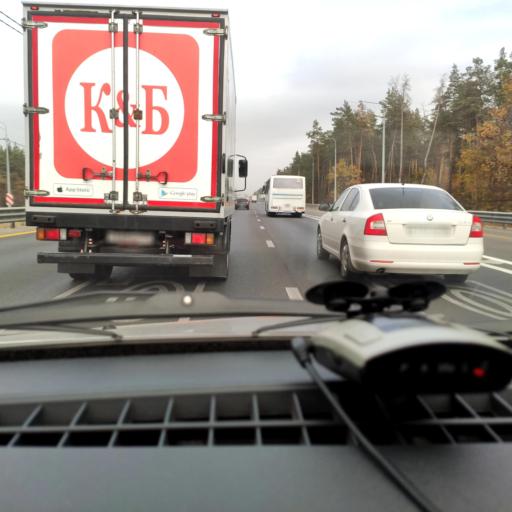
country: RU
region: Voronezj
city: Podgornoye
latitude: 51.7455
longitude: 39.1844
